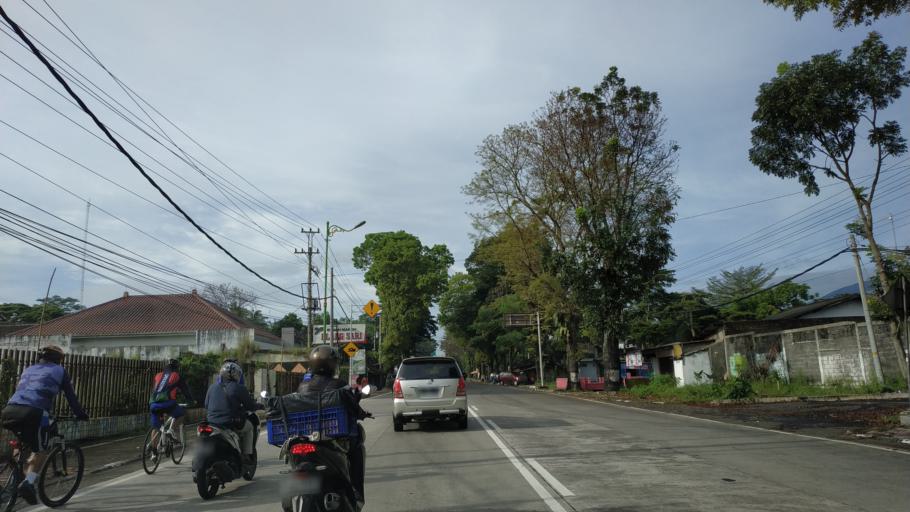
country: ID
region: Central Java
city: Salatiga
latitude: -7.3555
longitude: 110.5129
